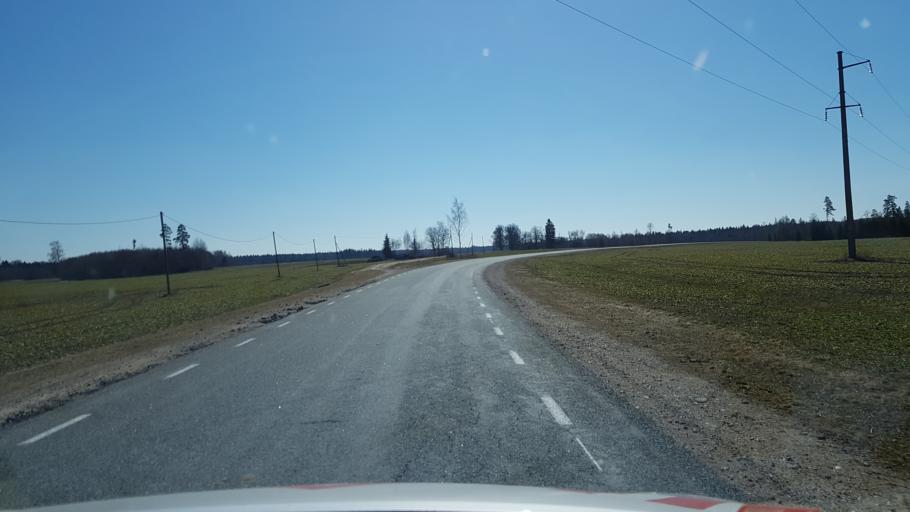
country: EE
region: Laeaene-Virumaa
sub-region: Rakke vald
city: Rakke
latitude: 59.0237
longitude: 26.3529
